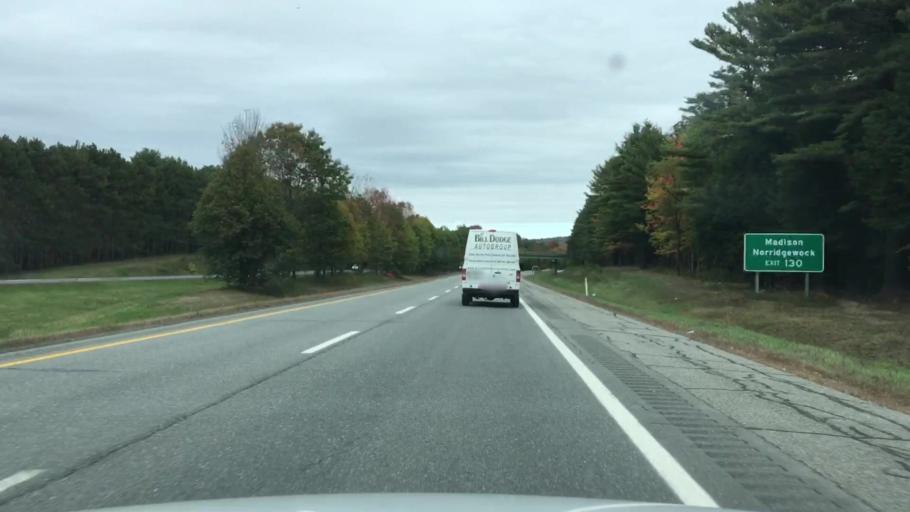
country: US
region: Maine
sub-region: Kennebec County
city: Waterville
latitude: 44.5637
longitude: -69.6705
